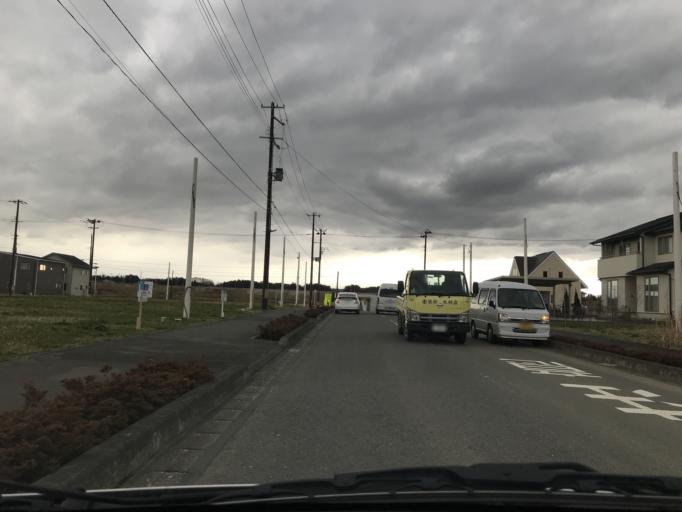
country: JP
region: Iwate
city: Mizusawa
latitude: 39.1209
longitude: 141.1633
